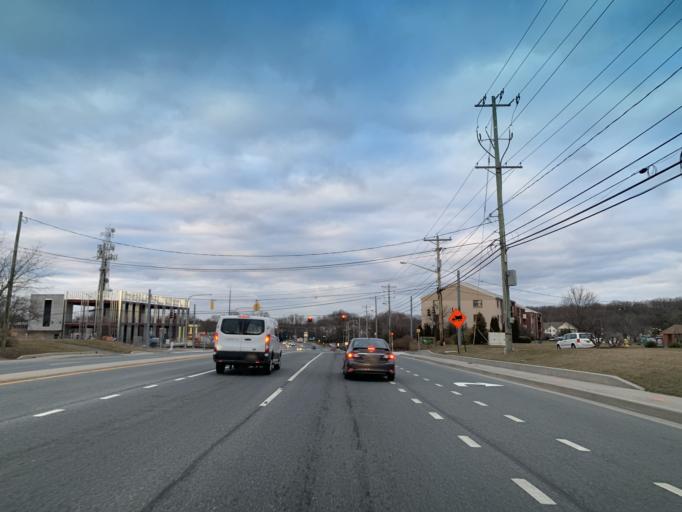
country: US
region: Delaware
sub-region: New Castle County
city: Bear
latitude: 39.6540
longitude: -75.6550
